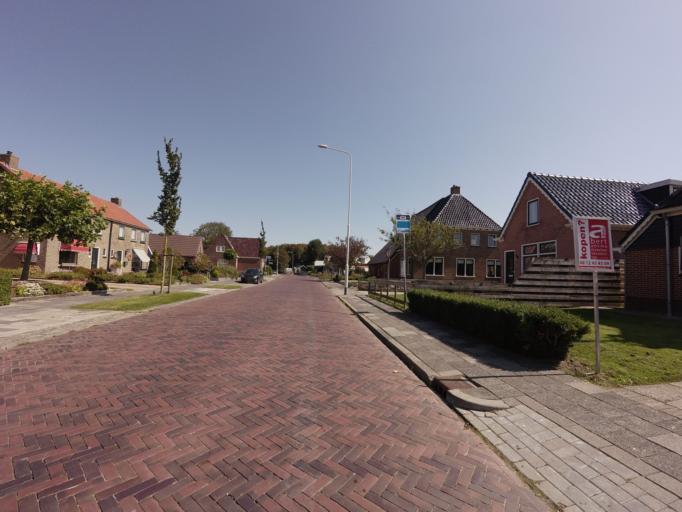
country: NL
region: Friesland
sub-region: Gemeente Dongeradeel
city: Anjum
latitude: 53.3808
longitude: 6.0521
